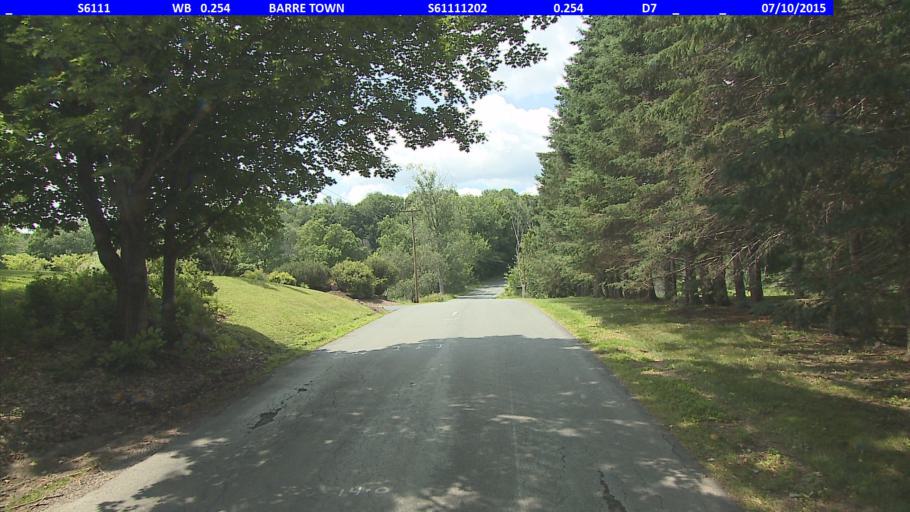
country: US
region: Vermont
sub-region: Washington County
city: Barre
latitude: 44.2233
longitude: -72.5049
